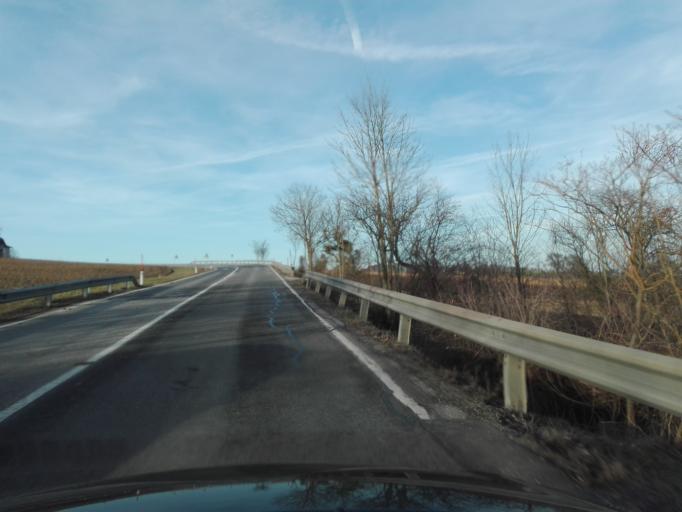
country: AT
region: Lower Austria
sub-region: Politischer Bezirk Amstetten
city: Strengberg
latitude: 48.1428
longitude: 14.6680
